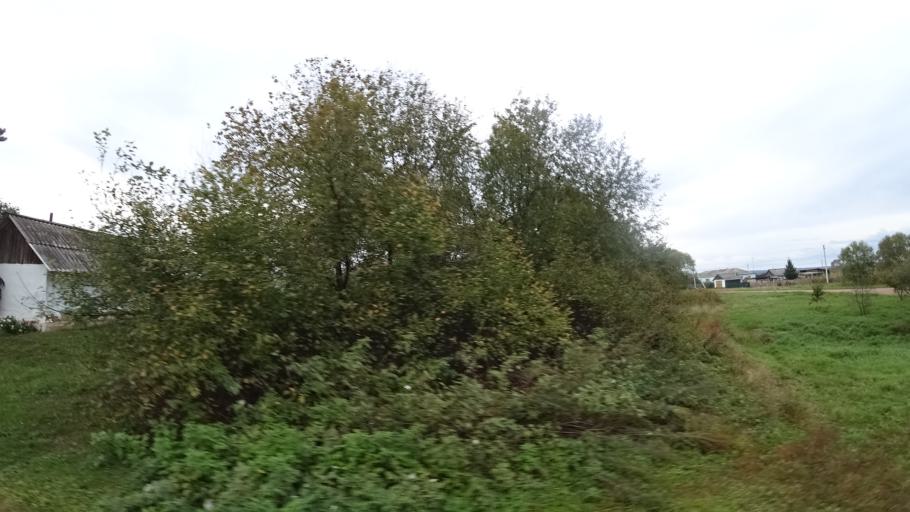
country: RU
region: Amur
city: Arkhara
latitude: 49.4345
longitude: 130.2652
